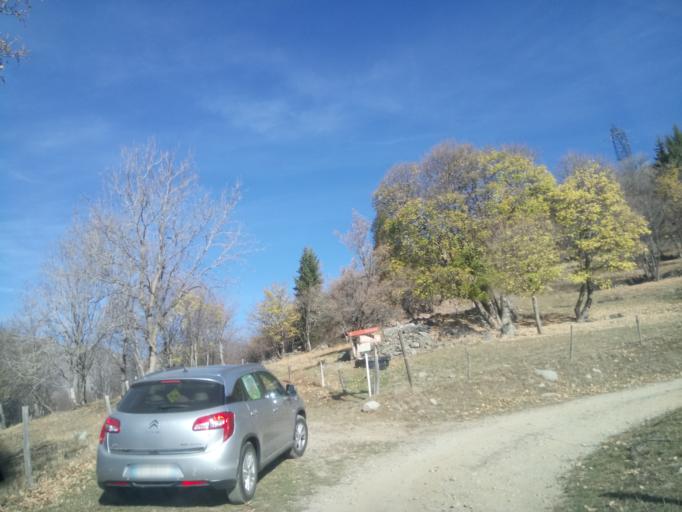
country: FR
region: Rhone-Alpes
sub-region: Departement de la Savoie
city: Saint-Michel-de-Maurienne
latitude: 45.2278
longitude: 6.4864
